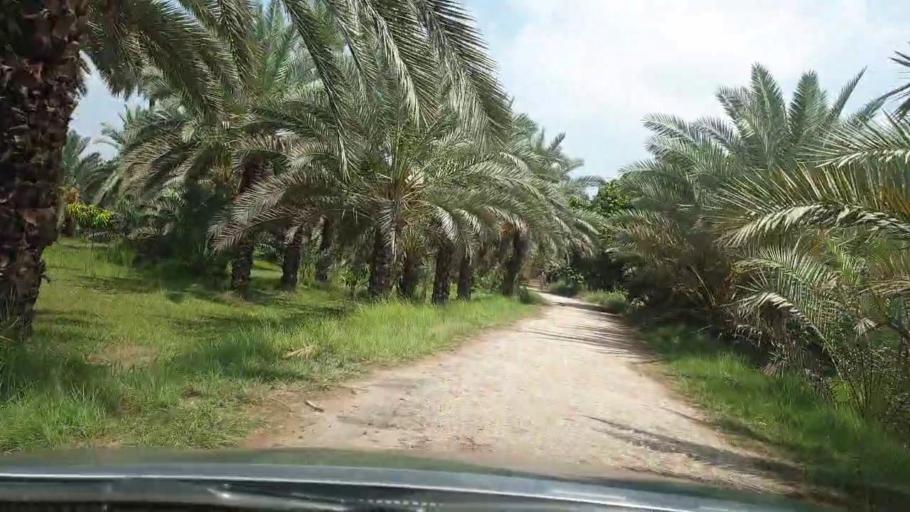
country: PK
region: Sindh
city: Pir jo Goth
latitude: 27.6142
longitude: 68.6666
